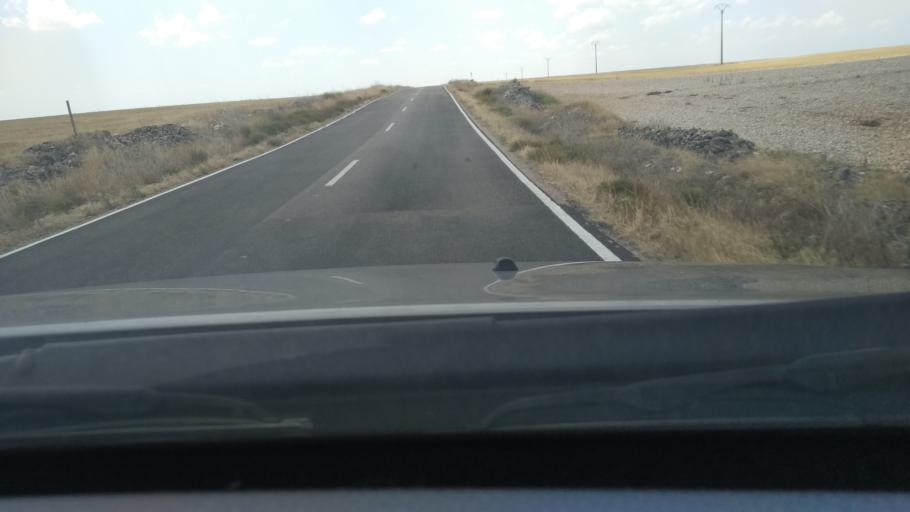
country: ES
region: Castille and Leon
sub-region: Provincia de Burgos
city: Iglesiarrubia
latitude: 41.9393
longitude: -3.8724
